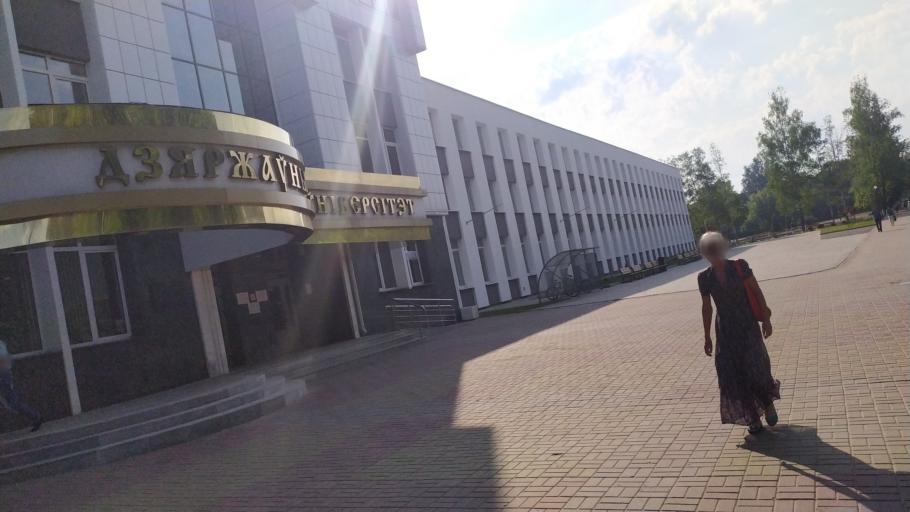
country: BY
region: Vitebsk
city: Navapolatsk
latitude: 55.5307
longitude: 28.6472
